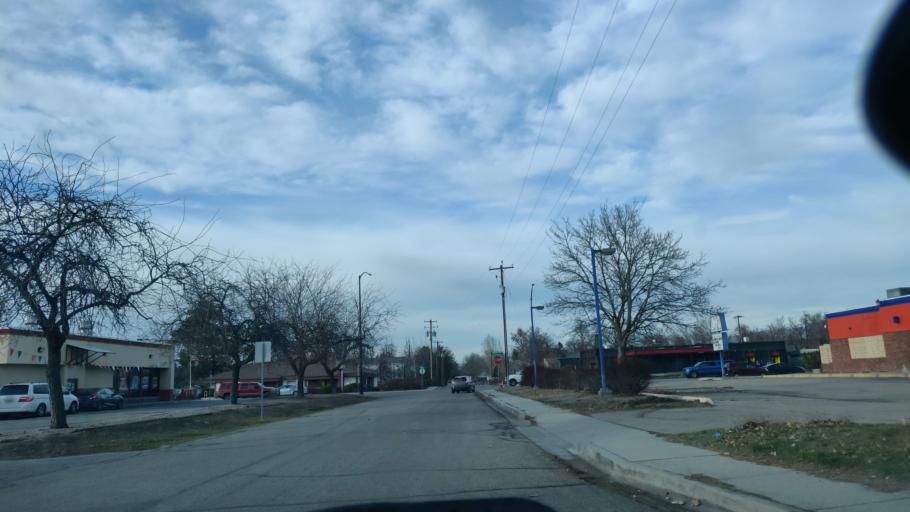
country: US
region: Idaho
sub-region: Ada County
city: Garden City
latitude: 43.6184
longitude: -116.2637
